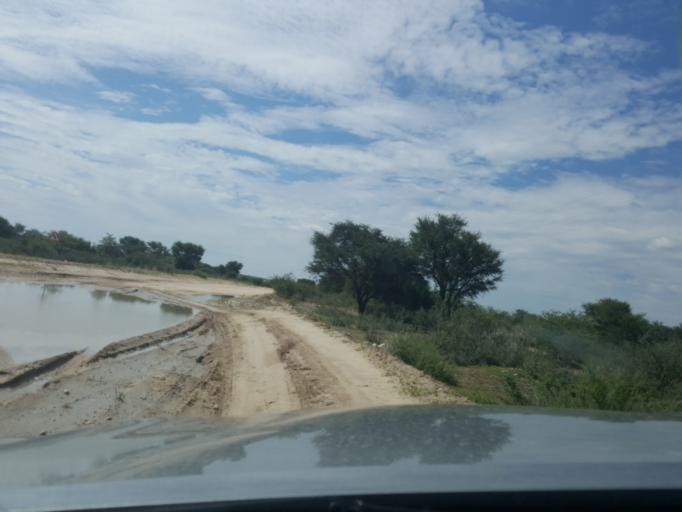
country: BW
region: Kweneng
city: Letlhakeng
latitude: -24.0646
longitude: 25.0308
